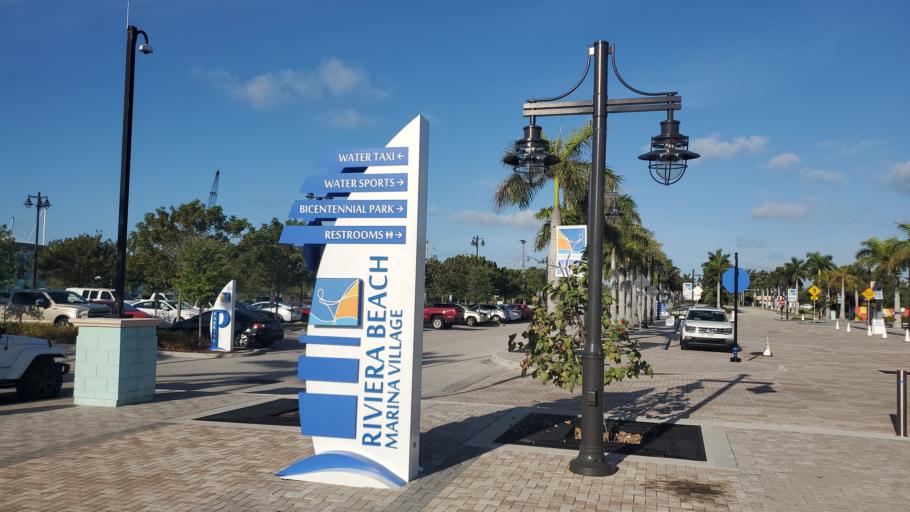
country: US
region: Florida
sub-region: Palm Beach County
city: Riviera Beach
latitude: 26.7738
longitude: -80.0523
